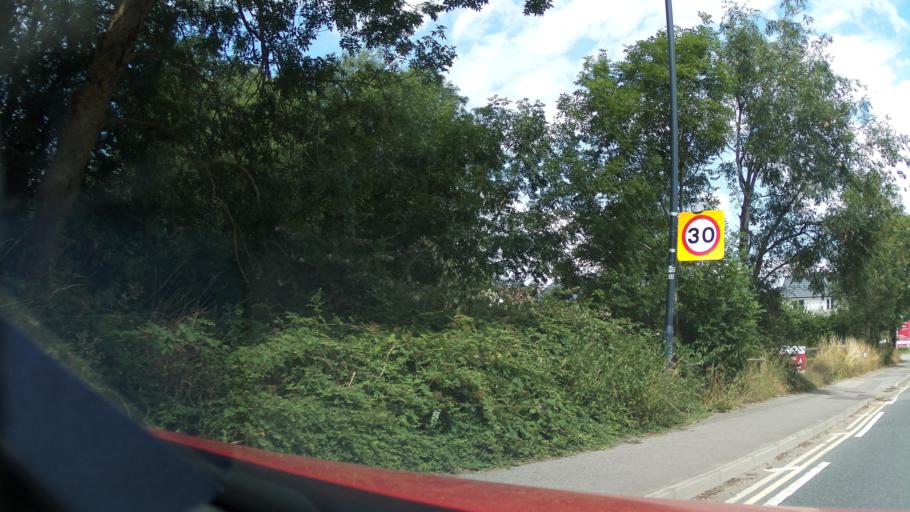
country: GB
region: England
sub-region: Borough of Swindon
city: Swindon
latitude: 51.5415
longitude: -1.7830
